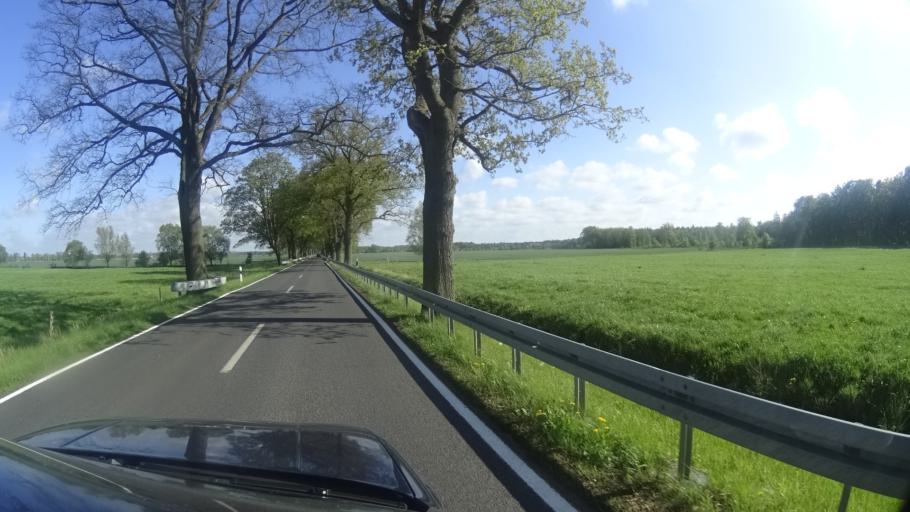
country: DE
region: Mecklenburg-Vorpommern
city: Gelbensande
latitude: 54.2485
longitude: 12.3132
